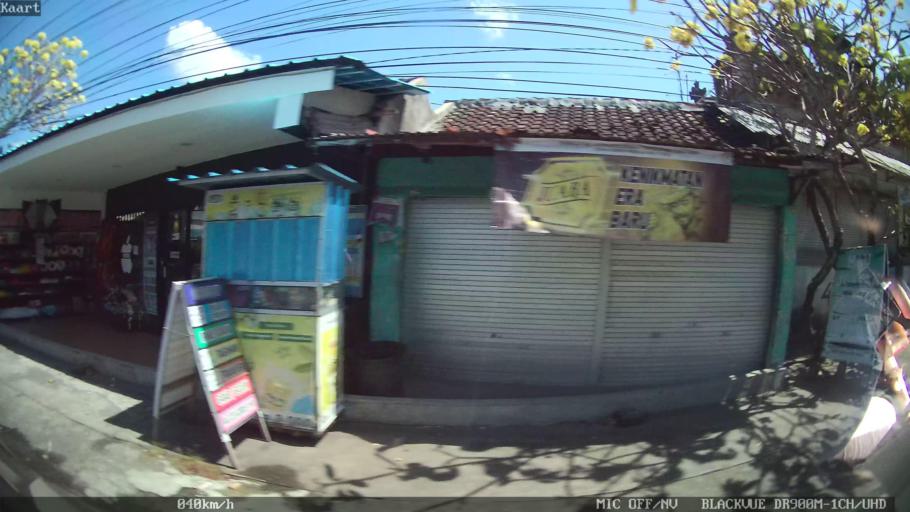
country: ID
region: Bali
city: Denpasar
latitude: -8.6632
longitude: 115.1760
